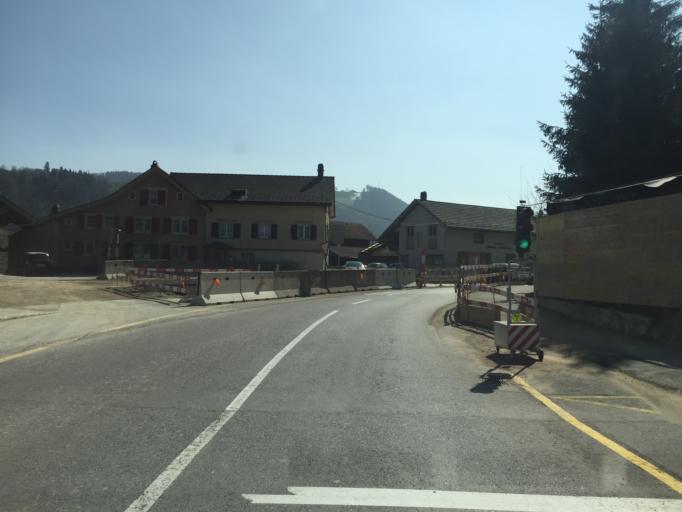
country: CH
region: Saint Gallen
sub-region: Wahlkreis Toggenburg
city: Buetschwil
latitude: 47.3696
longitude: 9.0763
